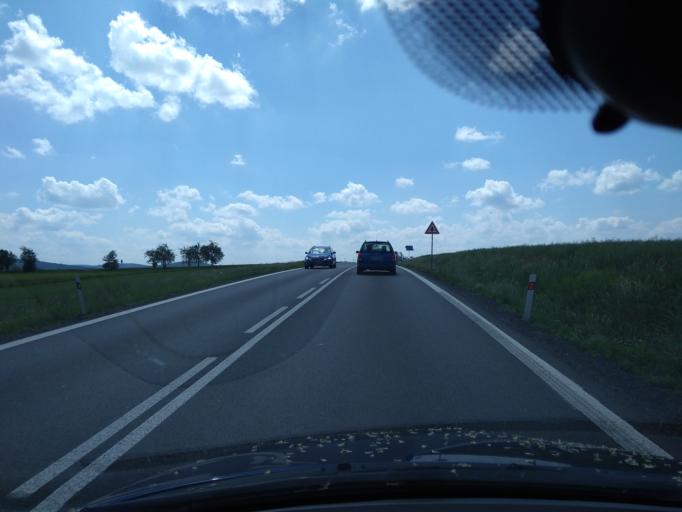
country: CZ
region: Plzensky
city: Prestice
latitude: 49.6024
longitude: 13.3255
